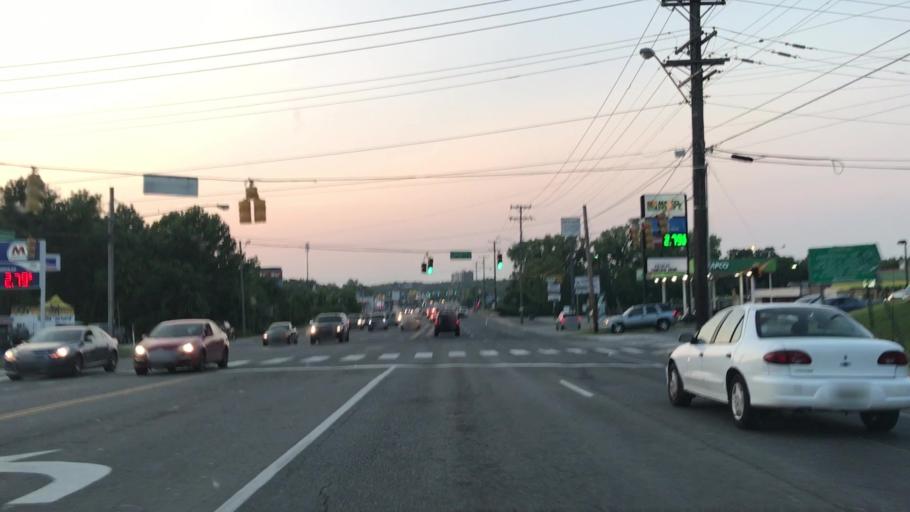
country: US
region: Tennessee
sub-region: Davidson County
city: Oak Hill
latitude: 36.0768
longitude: -86.7254
